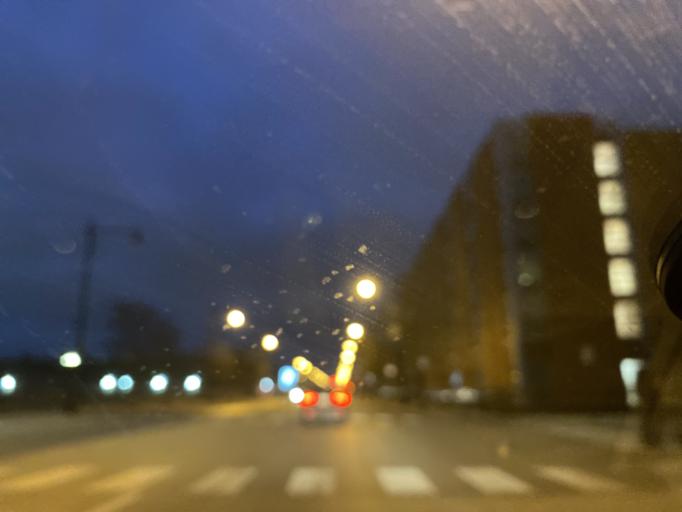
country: US
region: Illinois
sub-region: Cook County
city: Chicago
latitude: 41.7797
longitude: -87.6486
